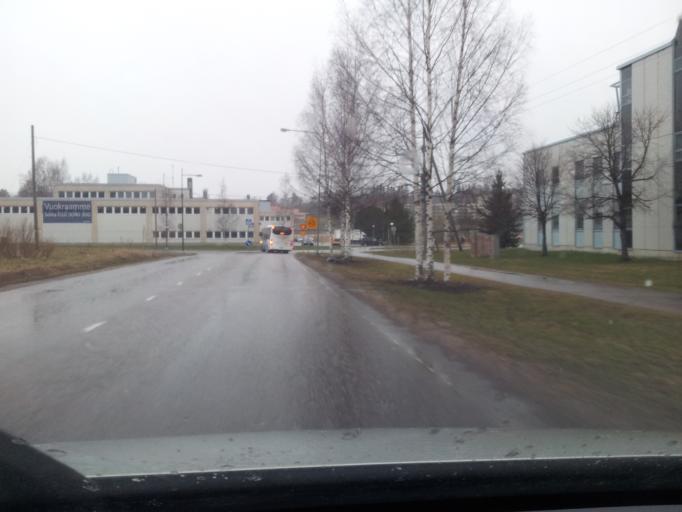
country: FI
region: Uusimaa
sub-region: Helsinki
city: Espoo
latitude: 60.1881
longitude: 24.6088
